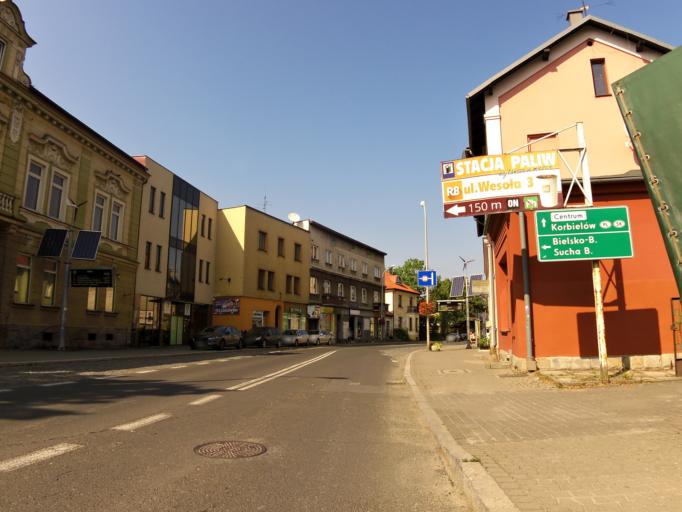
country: PL
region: Silesian Voivodeship
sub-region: Powiat zywiecki
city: Zywiec
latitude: 49.6838
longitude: 19.1904
